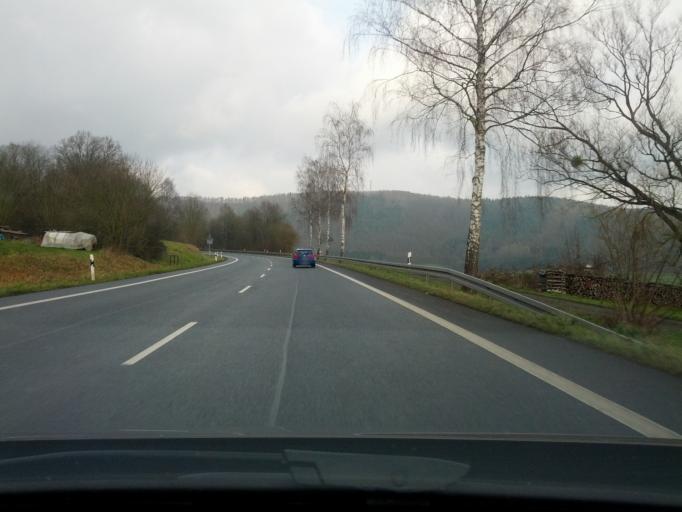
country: DE
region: Lower Saxony
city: Bodenfelde
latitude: 51.5874
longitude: 9.5828
